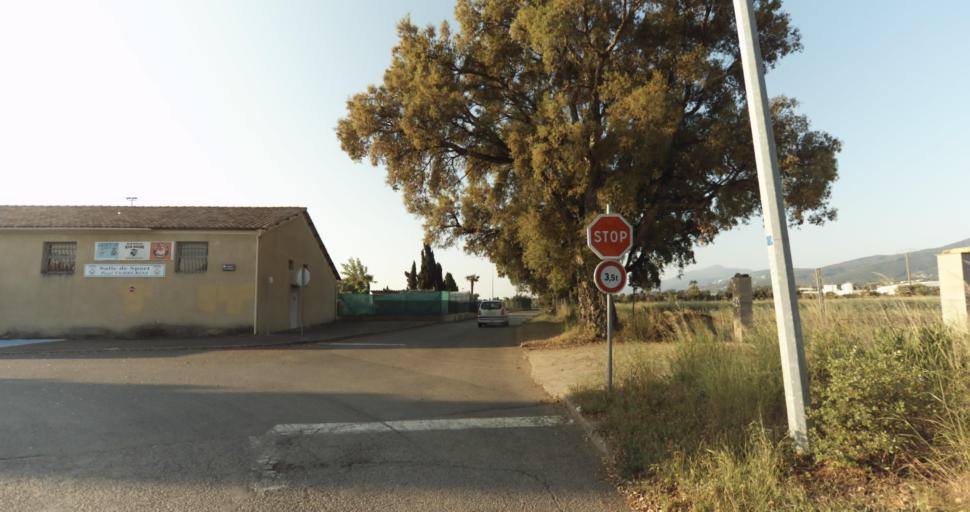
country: FR
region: Corsica
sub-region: Departement de la Haute-Corse
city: Biguglia
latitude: 42.6092
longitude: 9.4437
